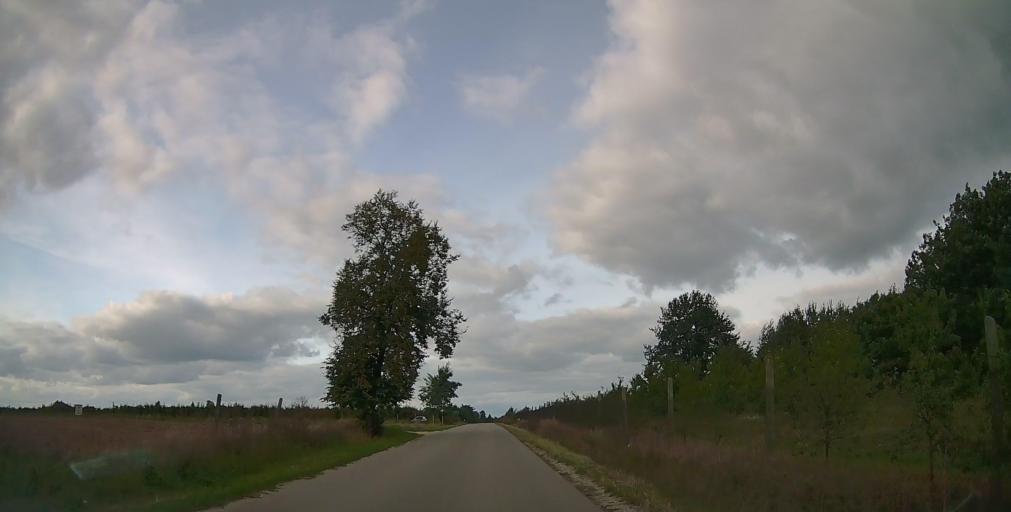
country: PL
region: Masovian Voivodeship
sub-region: Powiat bialobrzeski
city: Promna
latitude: 51.7167
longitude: 20.9584
